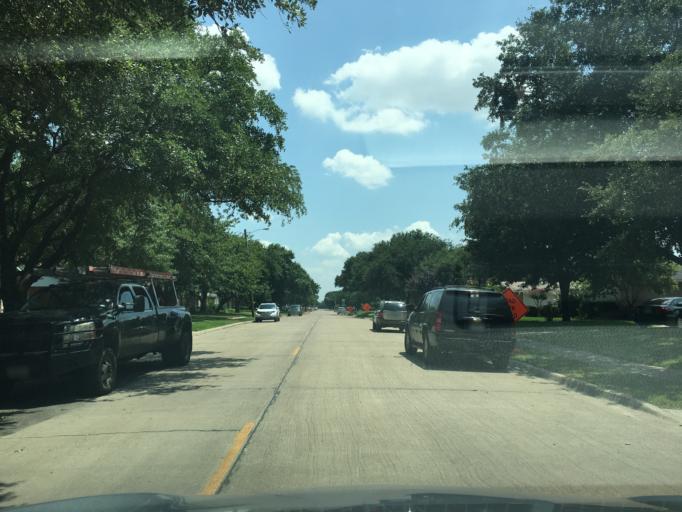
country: US
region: Texas
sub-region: Dallas County
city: Farmers Branch
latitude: 32.9131
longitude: -96.8640
